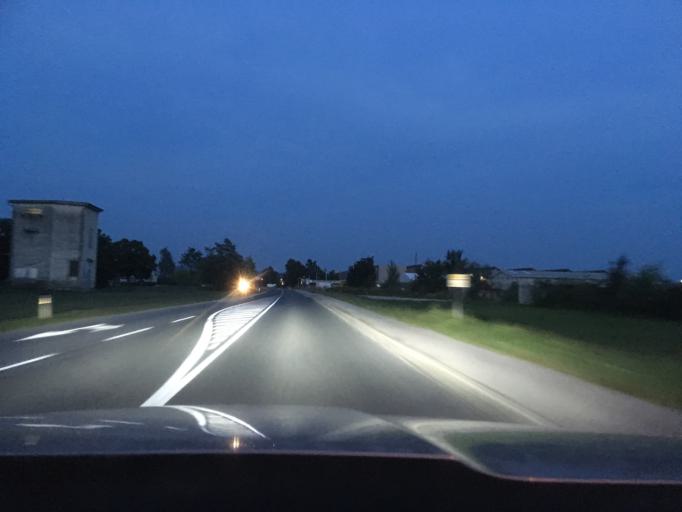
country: SI
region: Kamnik
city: Smarca
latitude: 46.2002
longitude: 14.5834
